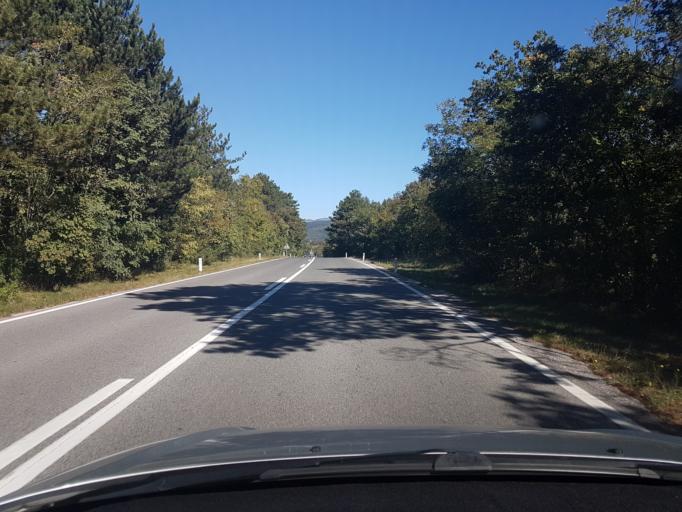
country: SI
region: Sezana
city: Sezana
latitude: 45.7308
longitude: 13.9173
